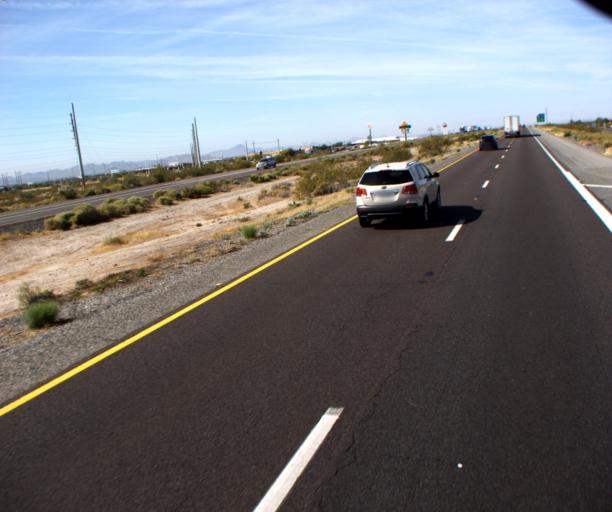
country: US
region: Arizona
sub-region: Maricopa County
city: Buckeye
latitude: 33.4351
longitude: -112.5868
